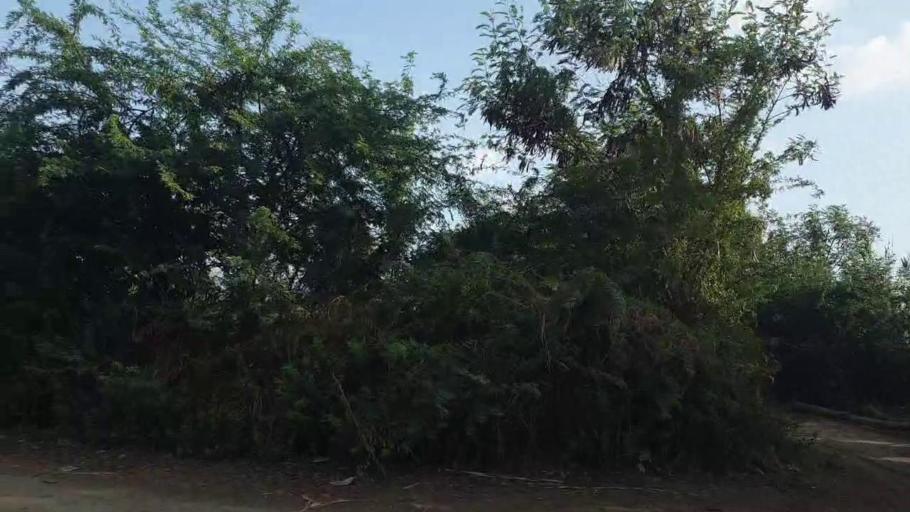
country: PK
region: Sindh
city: Kadhan
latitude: 24.6390
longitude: 69.1040
